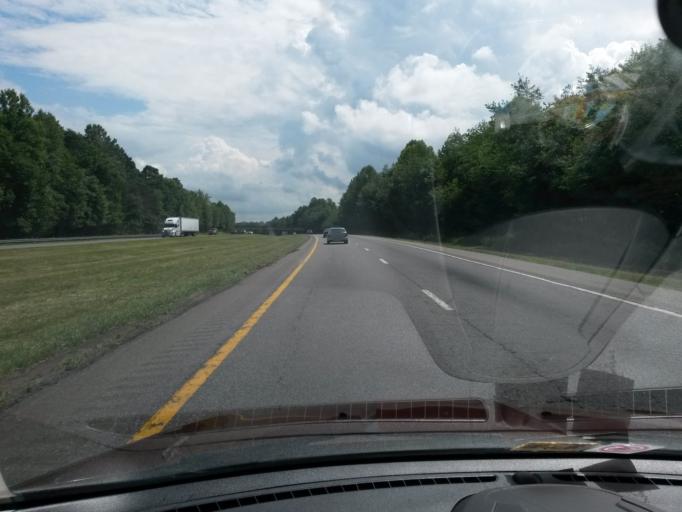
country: US
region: North Carolina
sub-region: Surry County
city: Dobson
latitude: 36.3670
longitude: -80.7967
